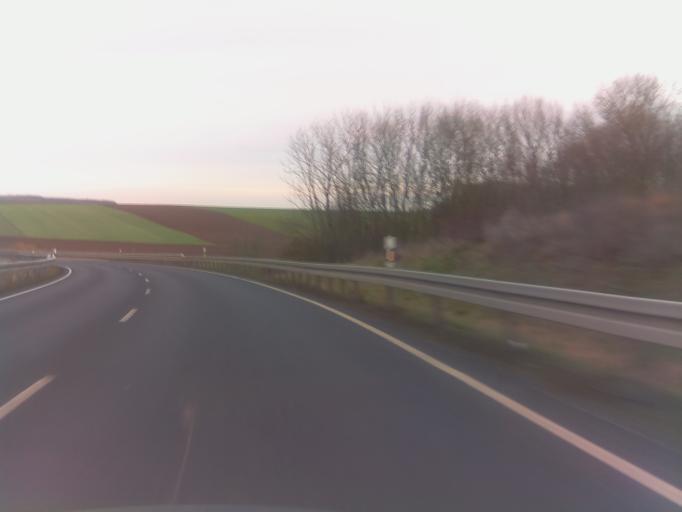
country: DE
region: Hesse
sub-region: Regierungsbezirk Kassel
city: Hunfeld
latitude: 50.6965
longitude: 9.7856
